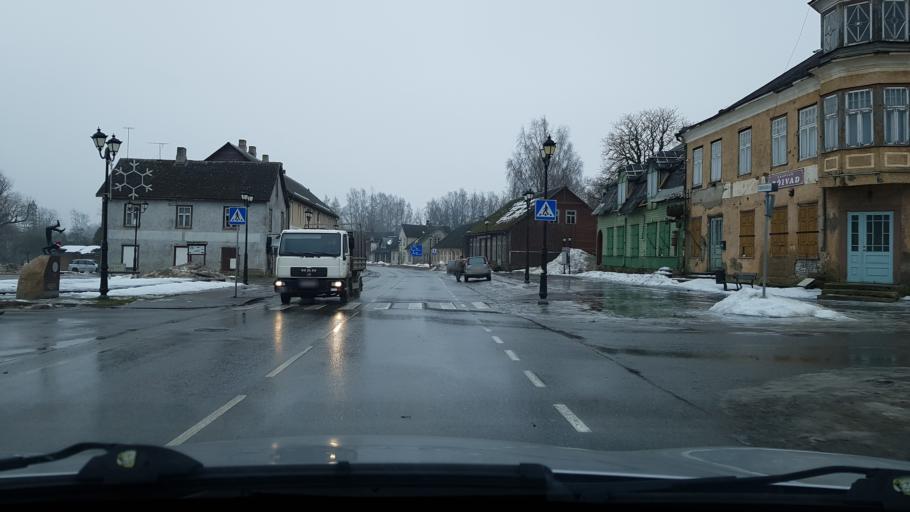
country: EE
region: Valgamaa
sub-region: Torva linn
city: Torva
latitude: 58.2363
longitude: 25.8605
